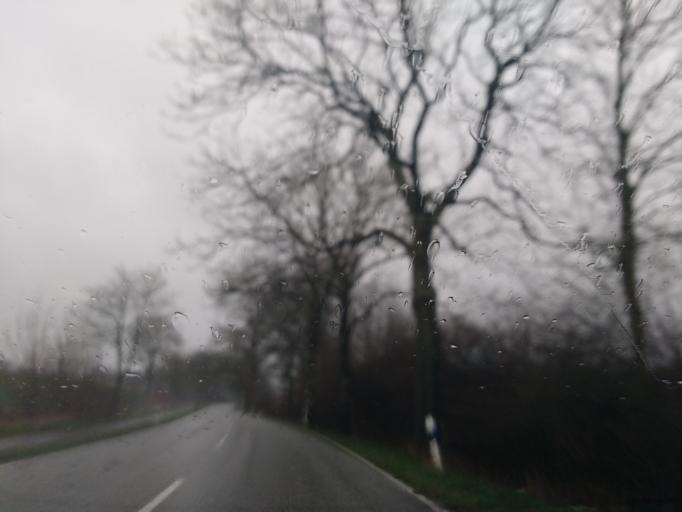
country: DE
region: Schleswig-Holstein
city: Blekendorf
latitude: 54.2908
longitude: 10.7120
